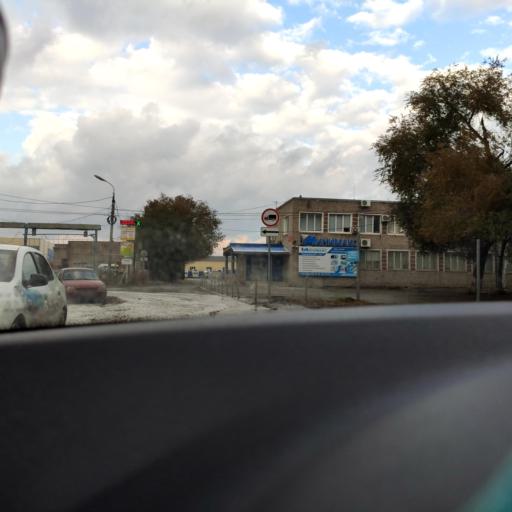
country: RU
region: Samara
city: Samara
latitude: 53.2011
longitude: 50.2549
